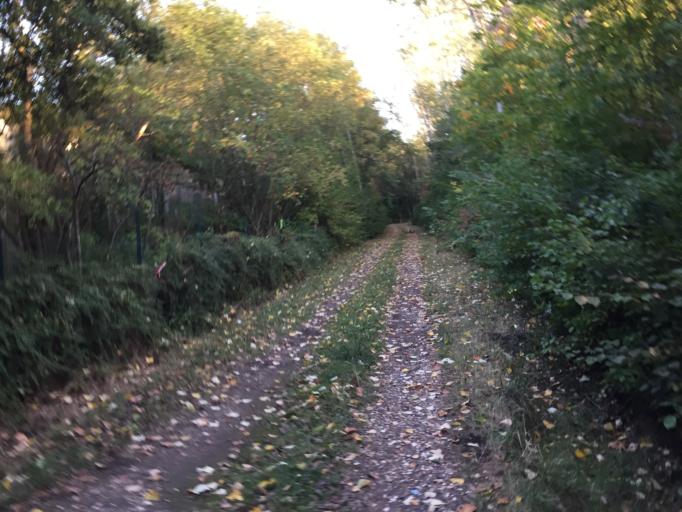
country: DE
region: Hesse
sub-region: Regierungsbezirk Giessen
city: Giessen
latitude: 50.5644
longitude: 8.6817
